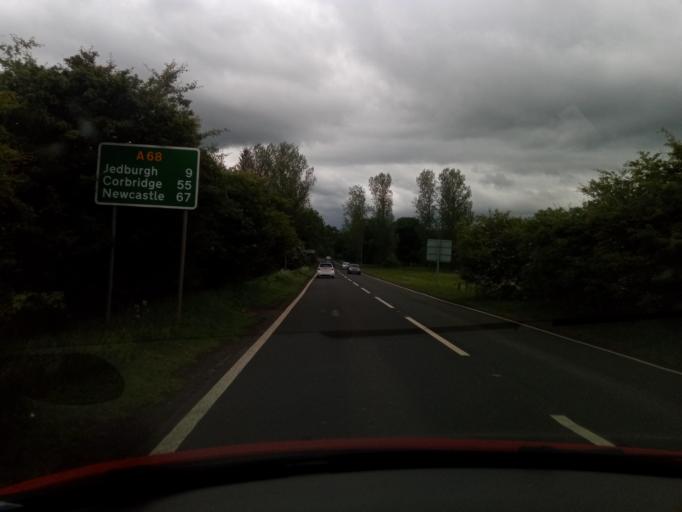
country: GB
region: Scotland
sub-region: The Scottish Borders
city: Saint Boswells
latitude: 55.5651
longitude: -2.6478
